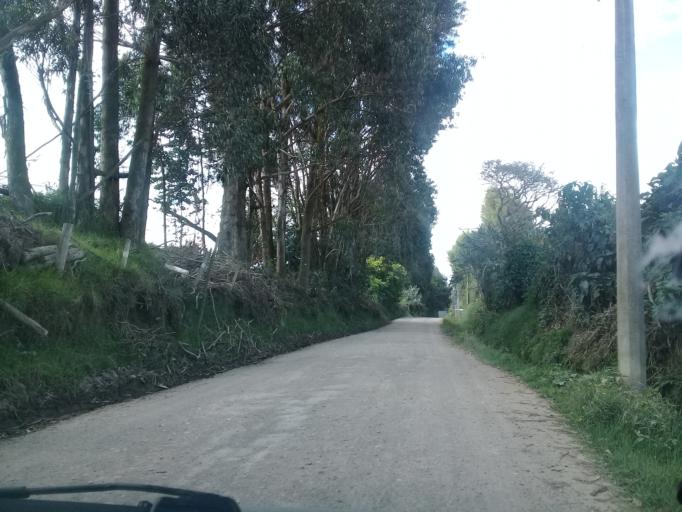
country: CO
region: Cundinamarca
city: El Rosal
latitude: 4.8662
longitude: -74.2167
